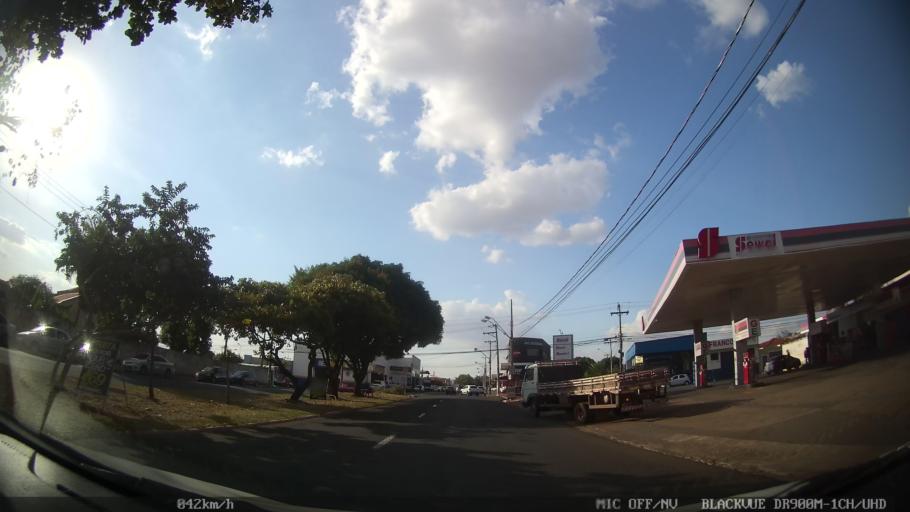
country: BR
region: Sao Paulo
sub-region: Ribeirao Preto
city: Ribeirao Preto
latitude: -21.1564
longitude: -47.8065
